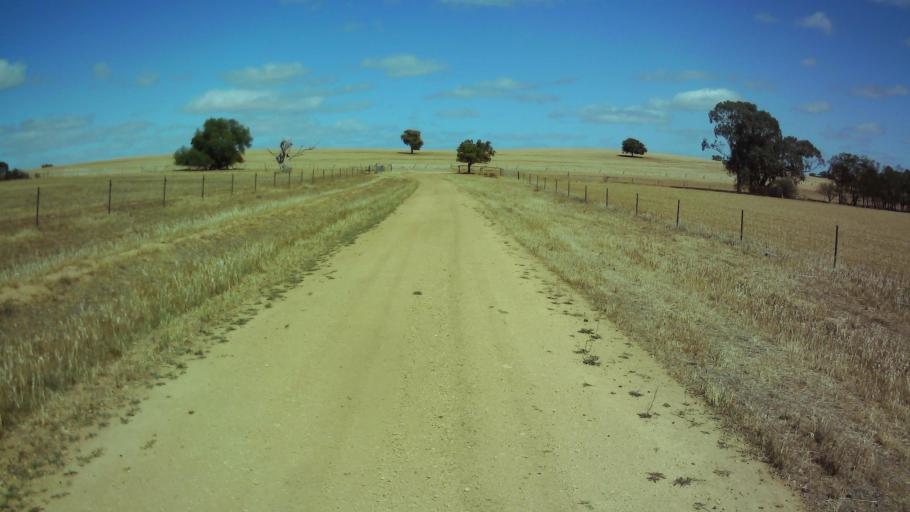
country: AU
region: New South Wales
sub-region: Weddin
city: Grenfell
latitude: -33.9795
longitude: 148.3849
